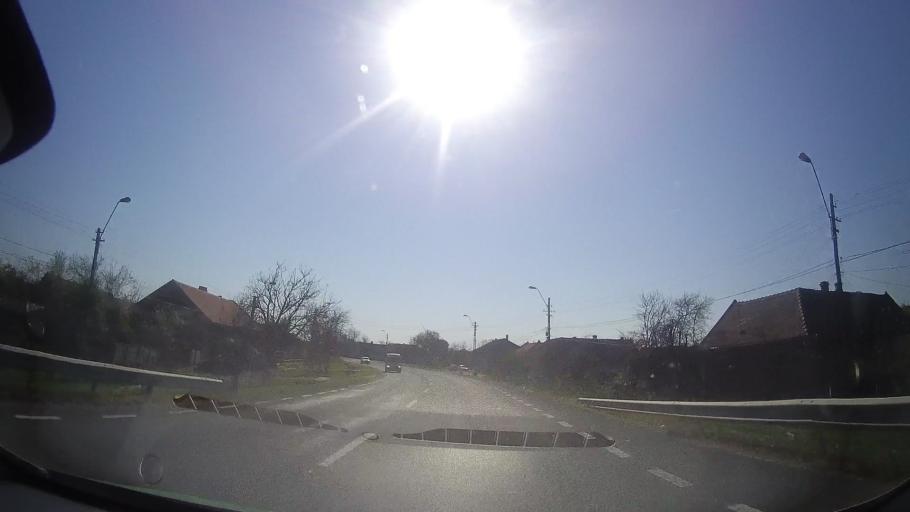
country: RO
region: Timis
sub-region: Comuna Belint
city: Belint
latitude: 45.7595
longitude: 21.7299
